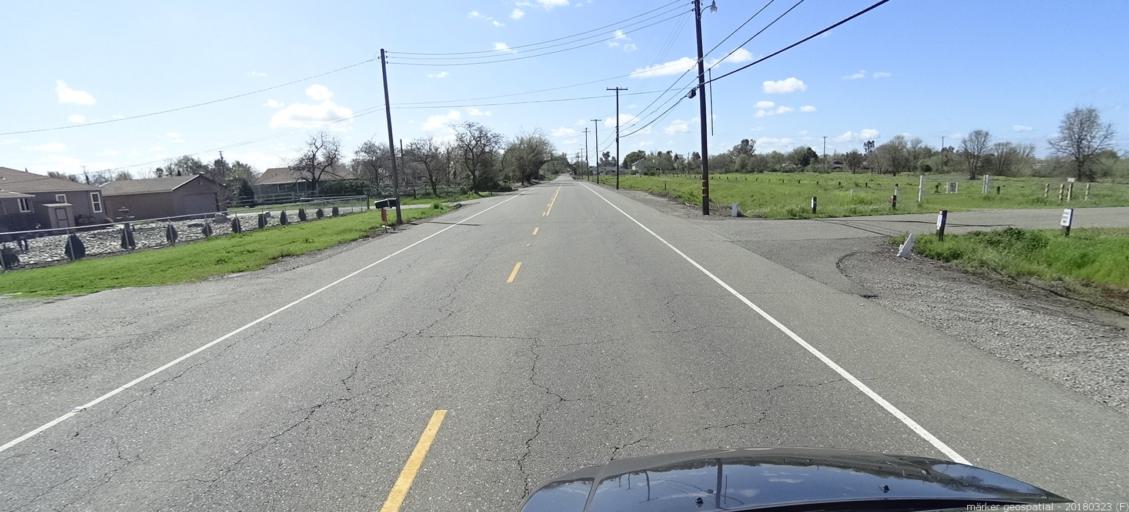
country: US
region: California
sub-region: Sacramento County
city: Rio Linda
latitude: 38.6707
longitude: -121.4384
